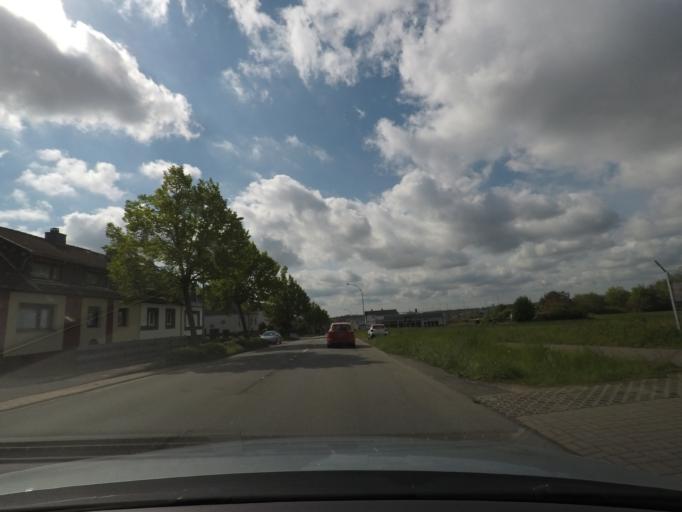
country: DE
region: Lower Saxony
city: Helmstedt
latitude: 52.2448
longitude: 10.9977
